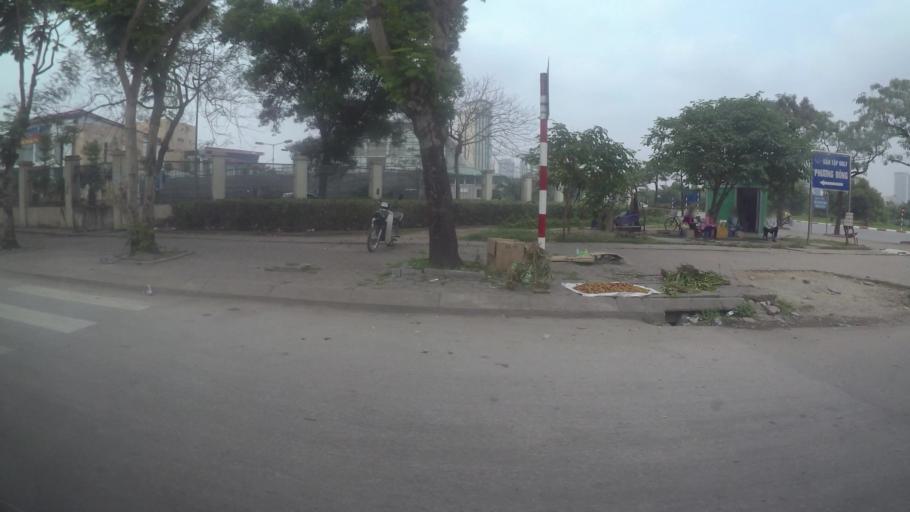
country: VN
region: Ha Noi
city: Cau Dien
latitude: 21.0241
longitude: 105.7662
